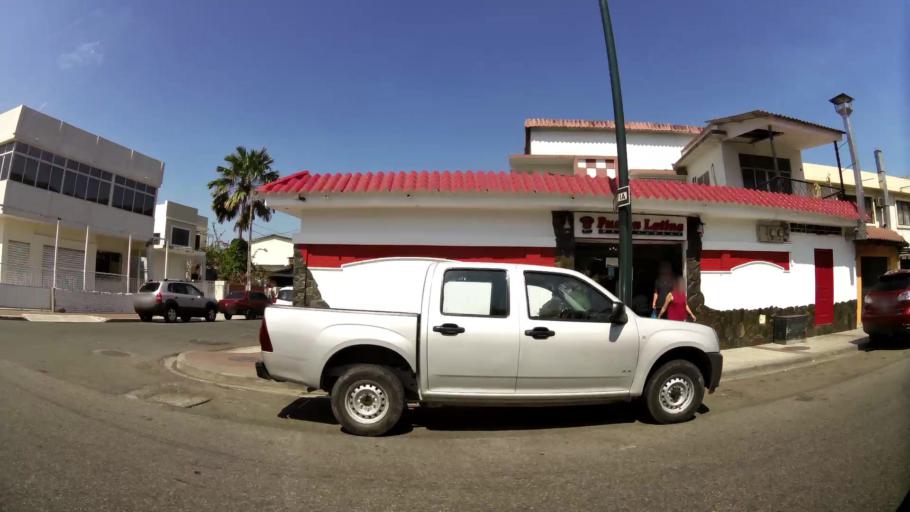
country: EC
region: Guayas
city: Guayaquil
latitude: -2.1654
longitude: -79.9209
